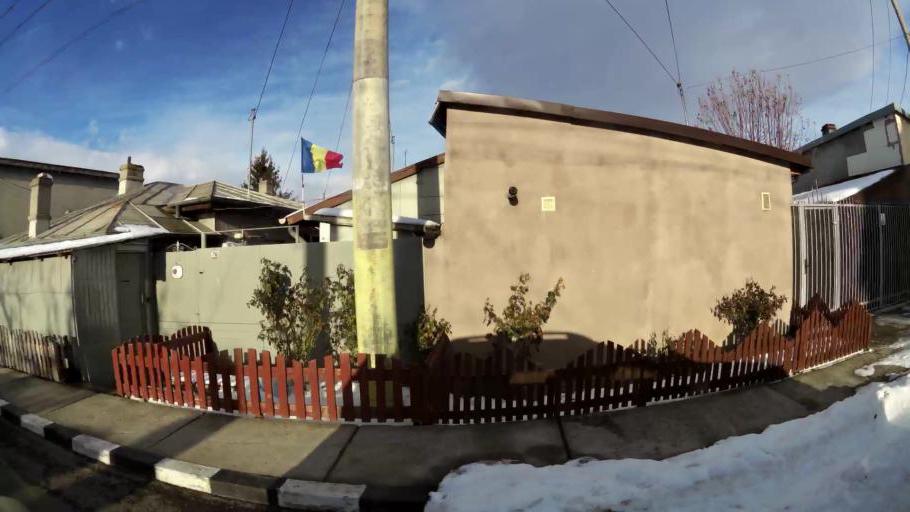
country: RO
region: Ilfov
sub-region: Comuna Fundeni-Dobroesti
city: Fundeni
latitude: 44.4626
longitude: 26.1654
